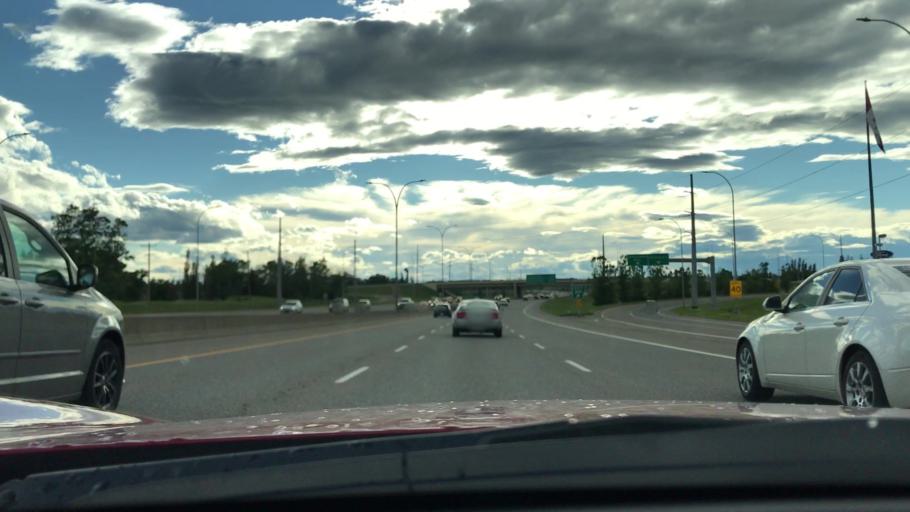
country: CA
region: Alberta
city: Calgary
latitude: 50.9477
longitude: -113.9988
